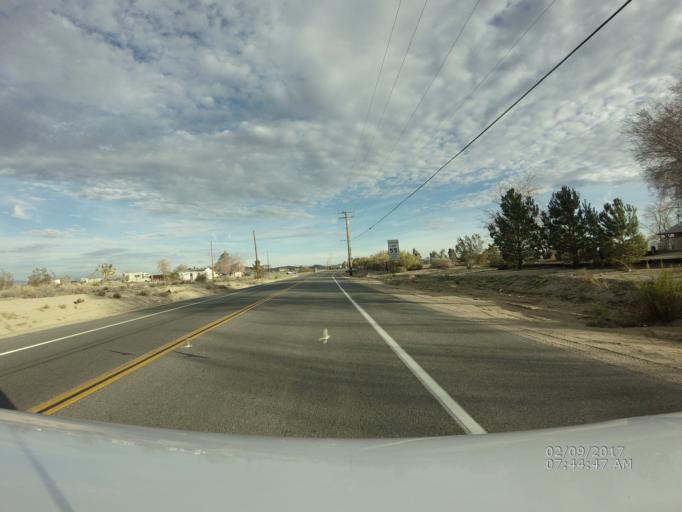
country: US
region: California
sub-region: Los Angeles County
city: Lake Los Angeles
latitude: 34.5427
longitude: -117.8354
